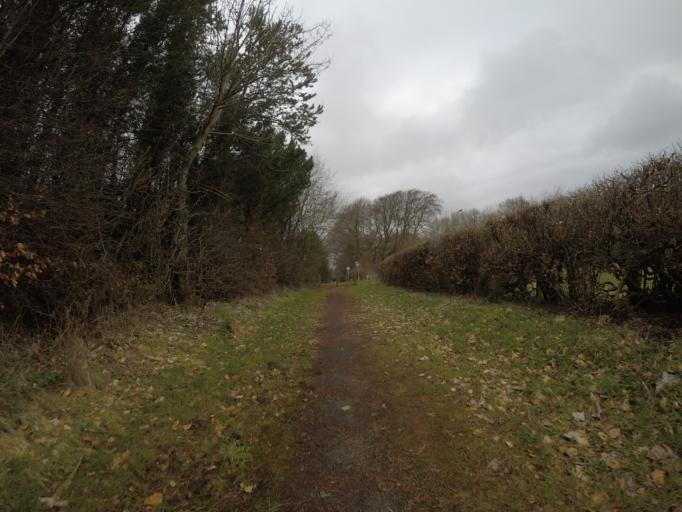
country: GB
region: Scotland
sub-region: North Ayrshire
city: Springside
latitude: 55.6268
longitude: -4.6147
